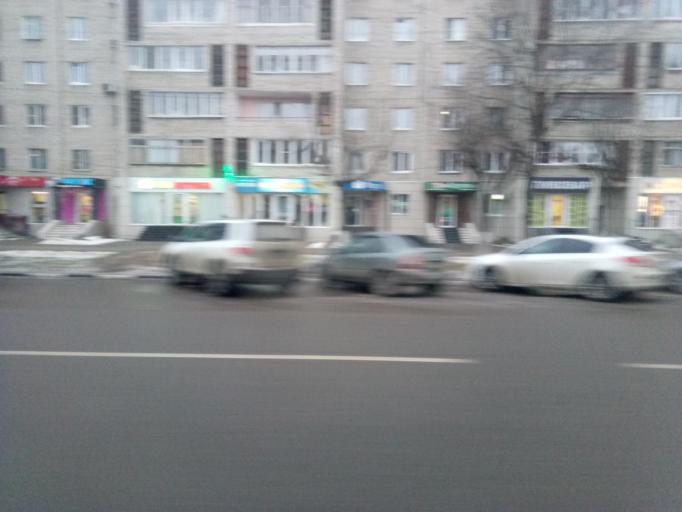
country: RU
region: Tula
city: Tula
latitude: 54.1963
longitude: 37.5902
